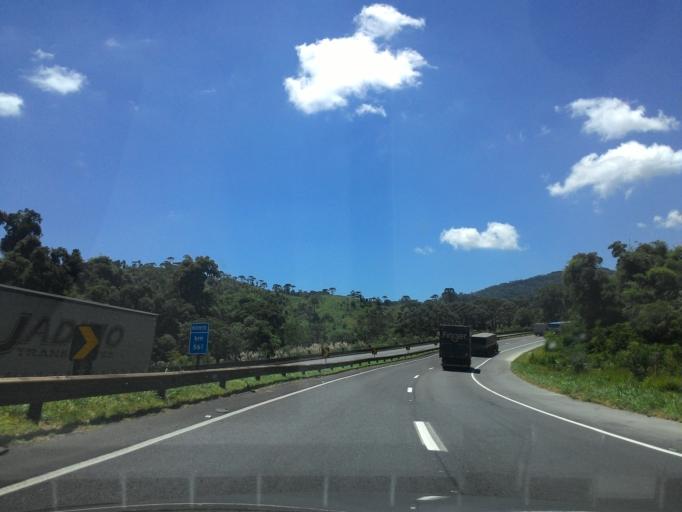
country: BR
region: Parana
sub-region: Antonina
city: Antonina
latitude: -25.0209
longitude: -48.5162
